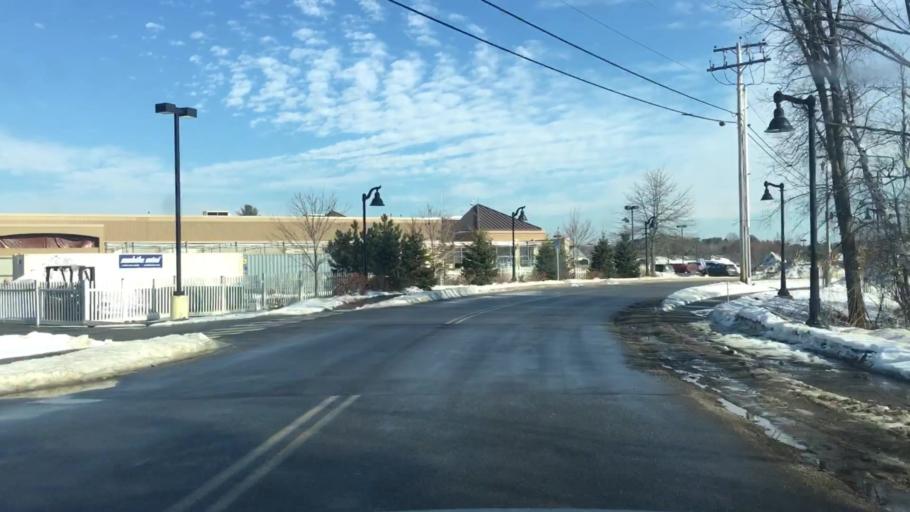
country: US
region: Maine
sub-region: Cumberland County
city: Falmouth
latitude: 43.7190
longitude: -70.2356
